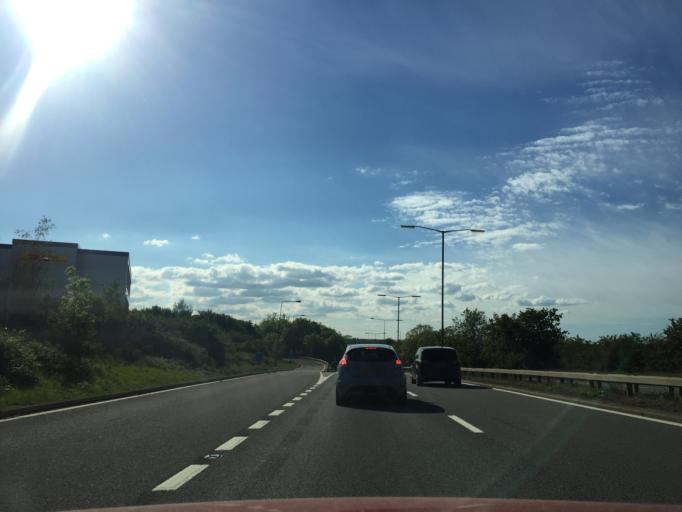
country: GB
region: England
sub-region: Warwickshire
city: Ryton on Dunsmore
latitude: 52.3724
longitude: -1.4521
